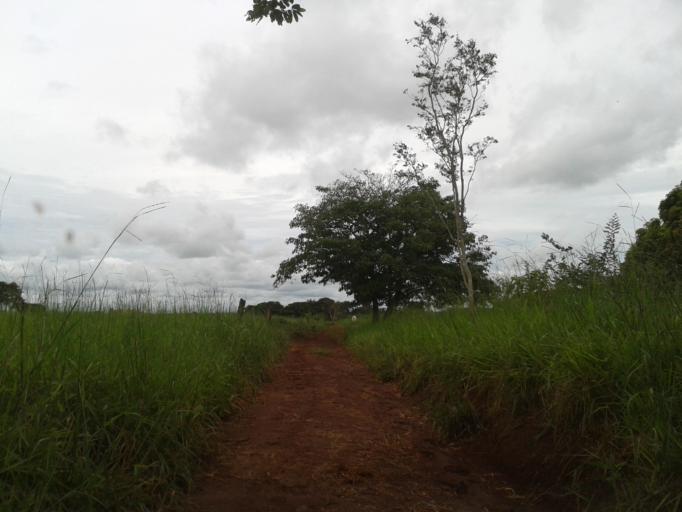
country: BR
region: Minas Gerais
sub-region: Capinopolis
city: Capinopolis
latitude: -18.7815
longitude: -49.7790
